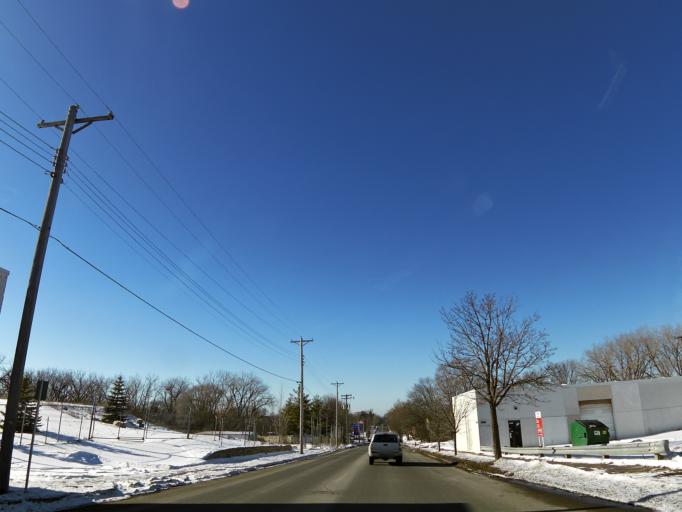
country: US
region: Minnesota
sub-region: Ramsey County
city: Maplewood
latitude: 44.9631
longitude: -93.0365
